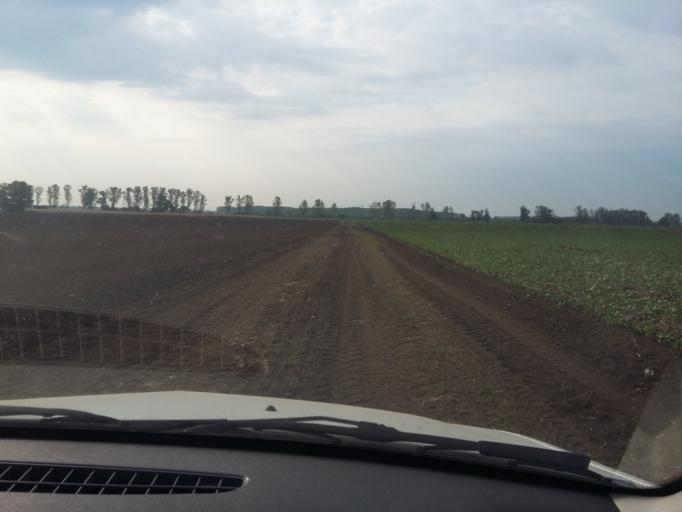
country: HU
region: Borsod-Abauj-Zemplen
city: Taktaharkany
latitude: 48.1234
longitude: 21.1075
